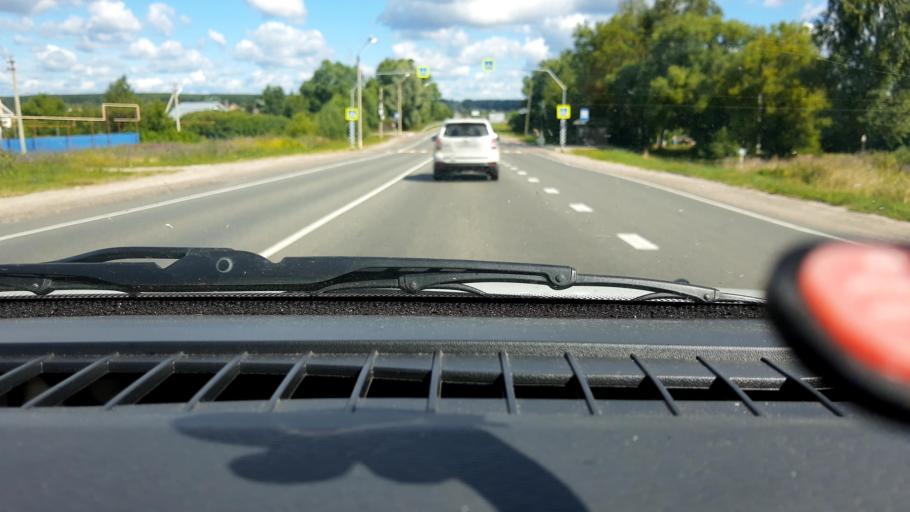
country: RU
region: Nizjnij Novgorod
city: Arzamas
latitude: 55.3292
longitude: 43.8880
